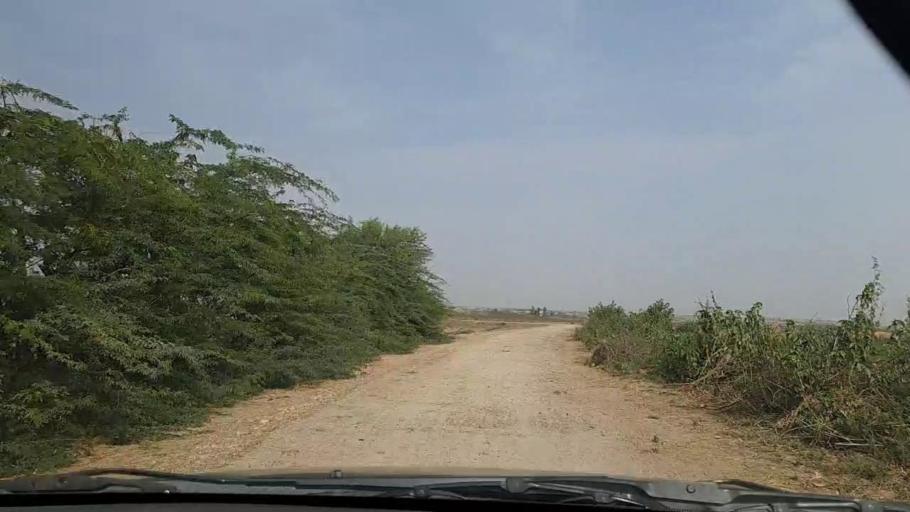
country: PK
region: Sindh
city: Thatta
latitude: 24.5742
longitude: 67.8518
